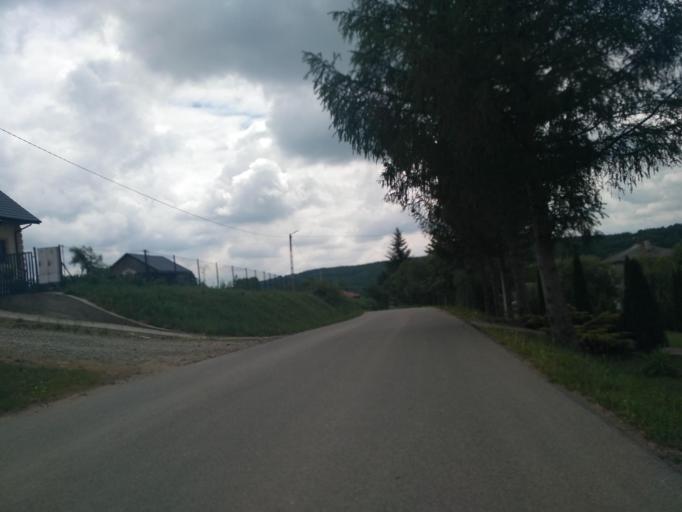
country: PL
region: Subcarpathian Voivodeship
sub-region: Powiat jasielski
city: Nowy Zmigrod
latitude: 49.6558
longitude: 21.5657
